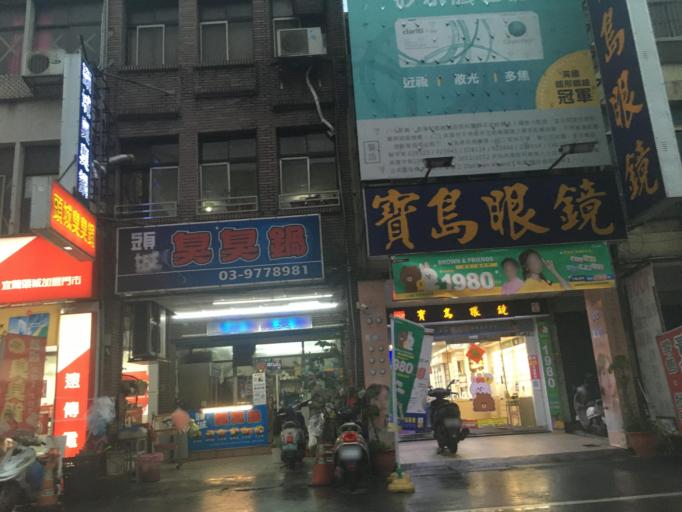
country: TW
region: Taiwan
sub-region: Yilan
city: Yilan
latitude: 24.8572
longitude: 121.8250
